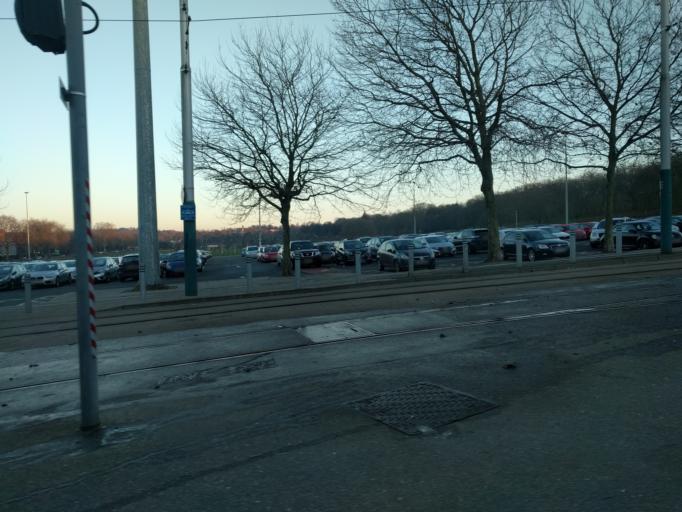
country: GB
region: England
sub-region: Nottingham
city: Nottingham
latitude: 52.9651
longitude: -1.1669
